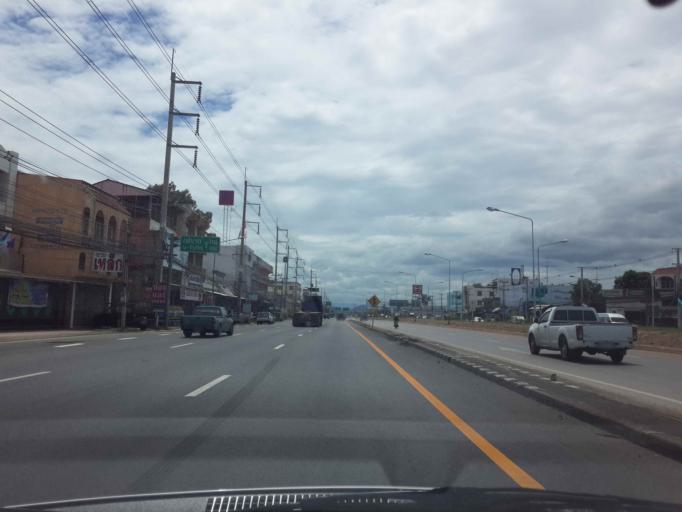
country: TH
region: Phetchaburi
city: Phetchaburi
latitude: 13.1141
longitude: 99.9269
